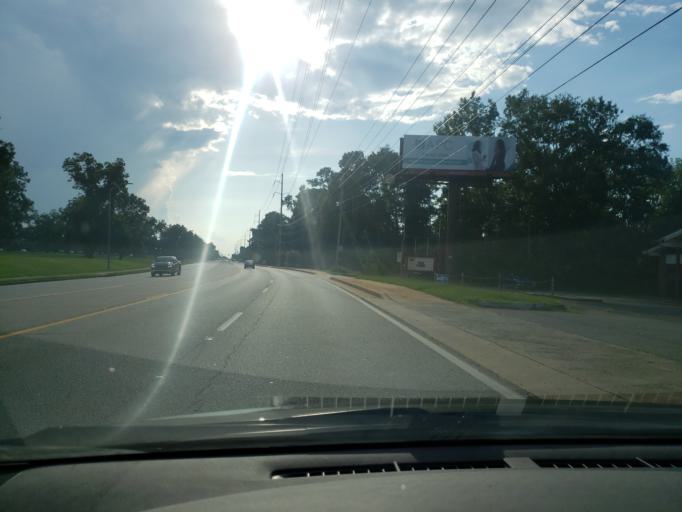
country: US
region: Georgia
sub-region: Dougherty County
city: Albany
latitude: 31.5859
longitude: -84.2083
